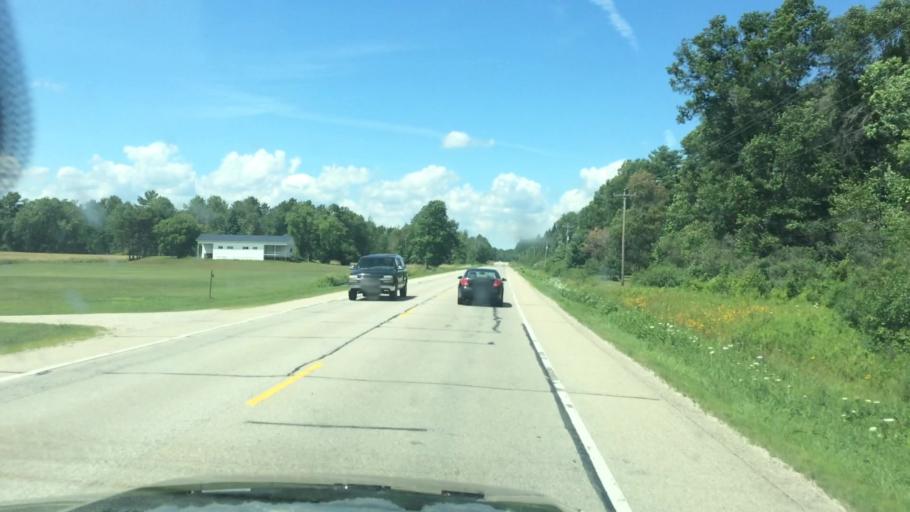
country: US
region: Wisconsin
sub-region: Marinette County
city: Peshtigo
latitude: 45.1001
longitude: -87.7242
